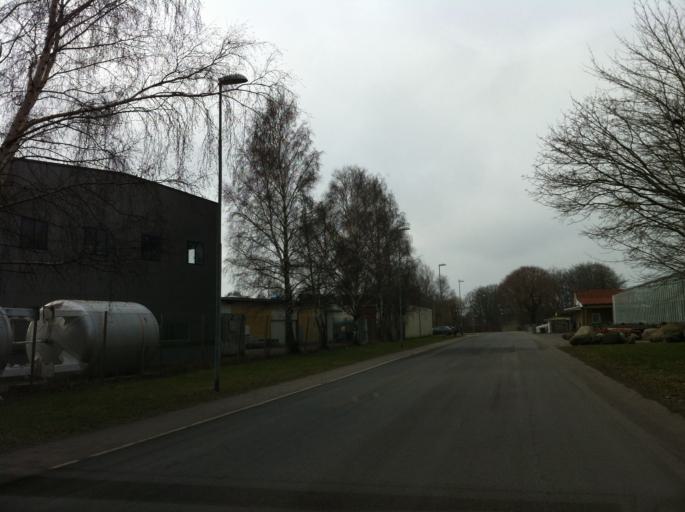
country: SE
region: Skane
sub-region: Kavlinge Kommun
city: Kaevlinge
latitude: 55.7863
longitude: 13.1325
